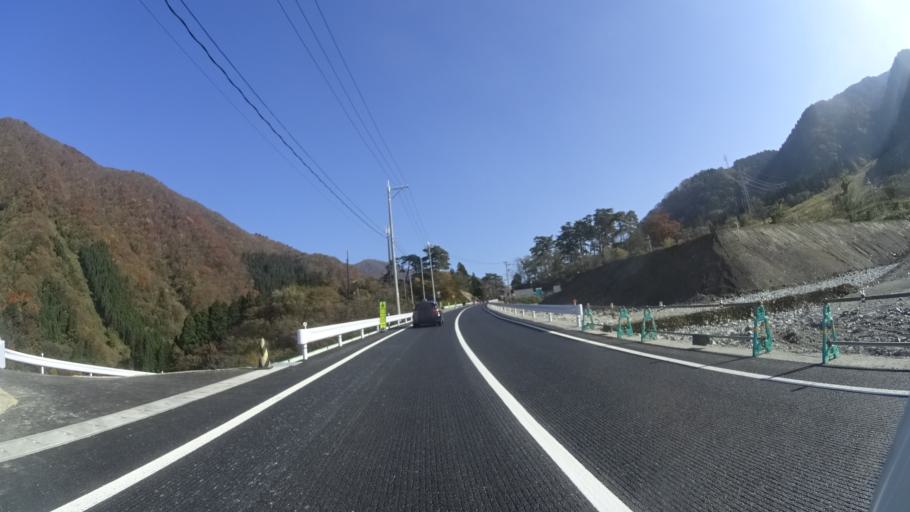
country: JP
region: Fukui
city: Ono
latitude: 35.9652
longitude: 136.6031
